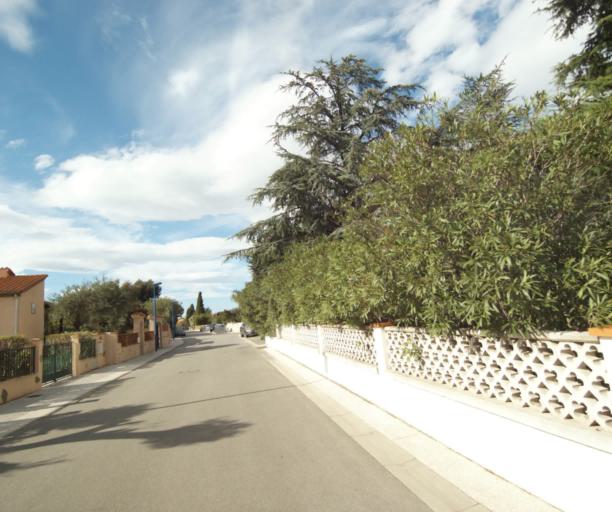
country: FR
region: Languedoc-Roussillon
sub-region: Departement des Pyrenees-Orientales
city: Argelers
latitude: 42.5454
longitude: 3.0118
